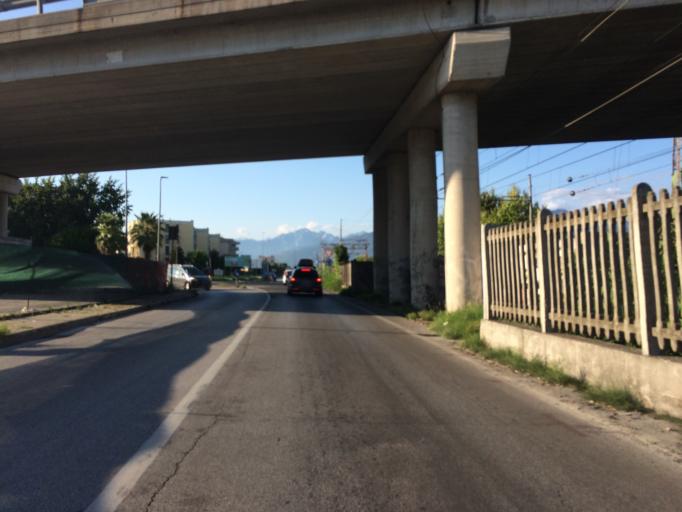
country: IT
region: Tuscany
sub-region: Provincia di Lucca
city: Viareggio
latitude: 43.8811
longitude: 10.2511
